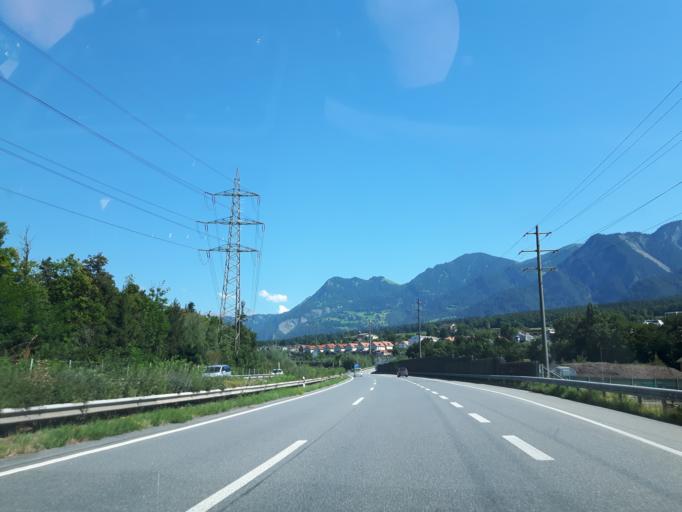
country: CH
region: Grisons
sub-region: Plessur District
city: Chur
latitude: 46.8711
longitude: 9.5287
